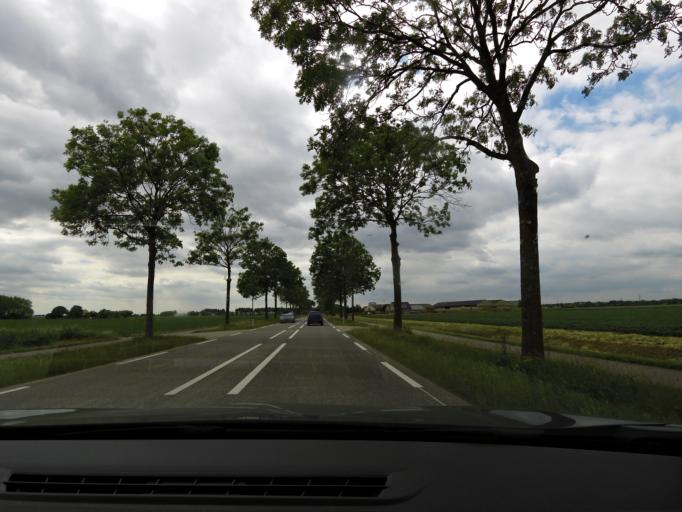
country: NL
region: North Brabant
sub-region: Gemeente Moerdijk
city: Klundert
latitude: 51.6472
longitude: 4.6368
